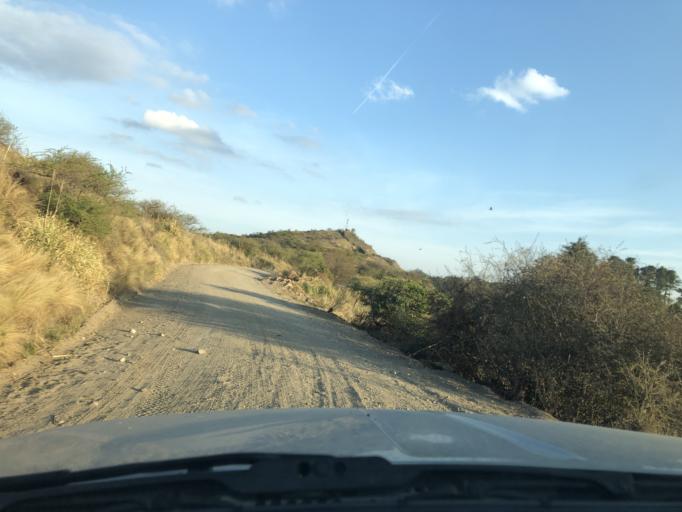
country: AR
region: Cordoba
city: Agua de Oro
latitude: -31.0609
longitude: -64.3483
